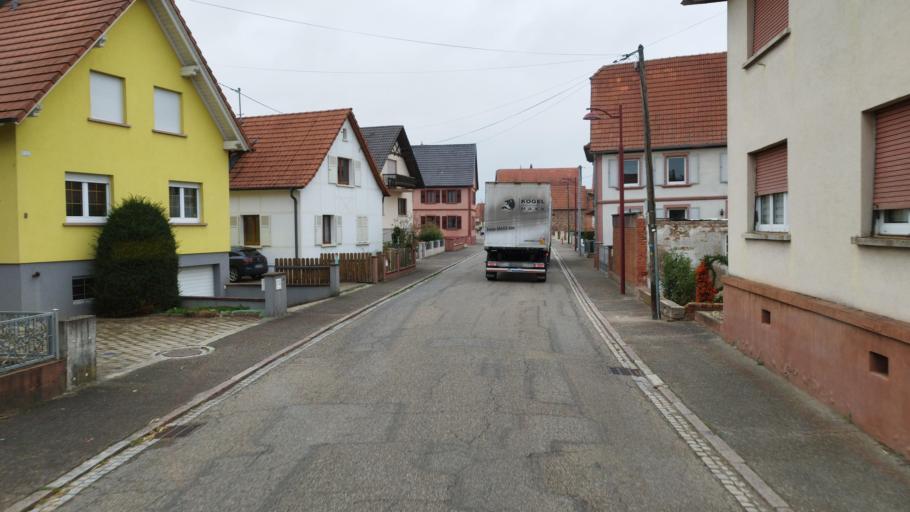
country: DE
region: Rheinland-Pfalz
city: Kapsweyer
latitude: 48.9911
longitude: 8.0328
